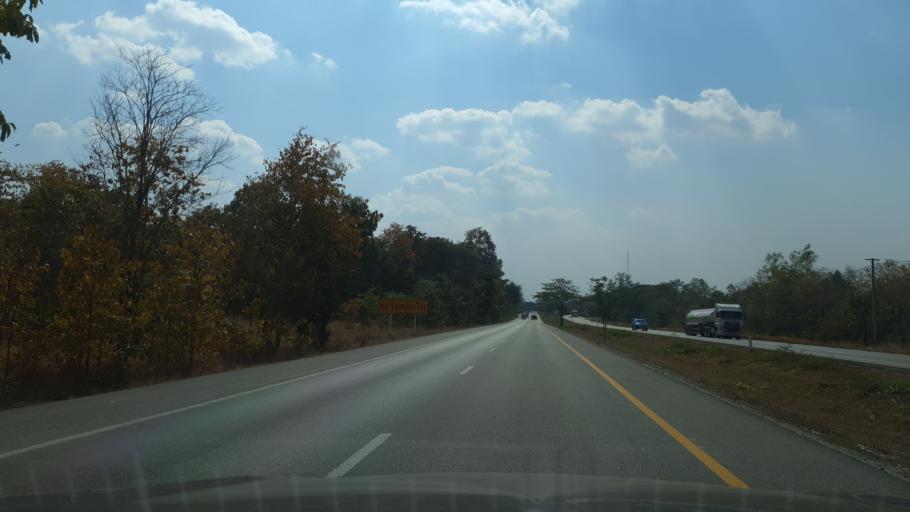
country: TH
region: Lampang
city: Mae Phrik
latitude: 17.3136
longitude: 99.1498
